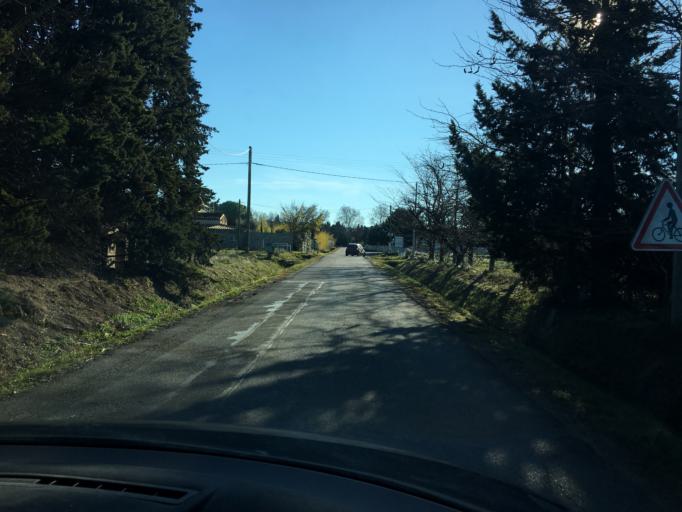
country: FR
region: Provence-Alpes-Cote d'Azur
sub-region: Departement des Bouches-du-Rhone
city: Maillane
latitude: 43.7988
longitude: 4.7887
